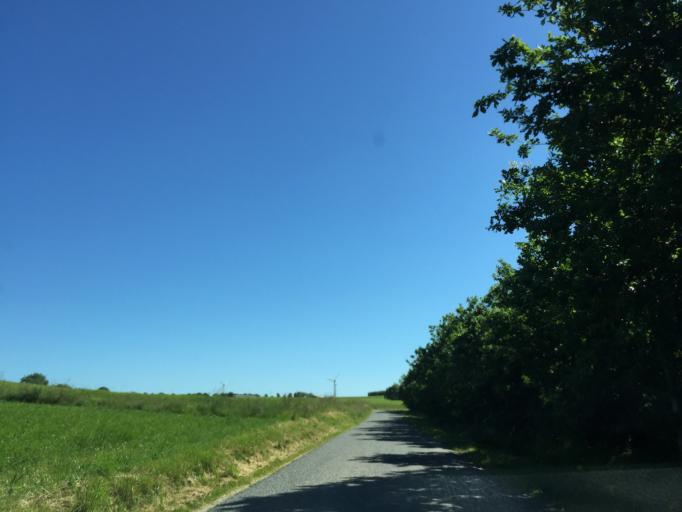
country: DK
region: Central Jutland
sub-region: Viborg Kommune
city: Bjerringbro
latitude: 56.2688
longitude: 9.6920
